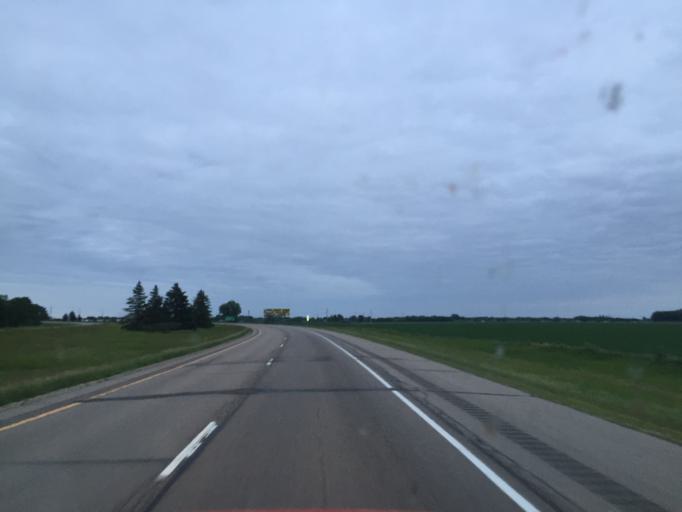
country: US
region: Minnesota
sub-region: Mower County
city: Austin
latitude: 43.6596
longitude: -93.0330
